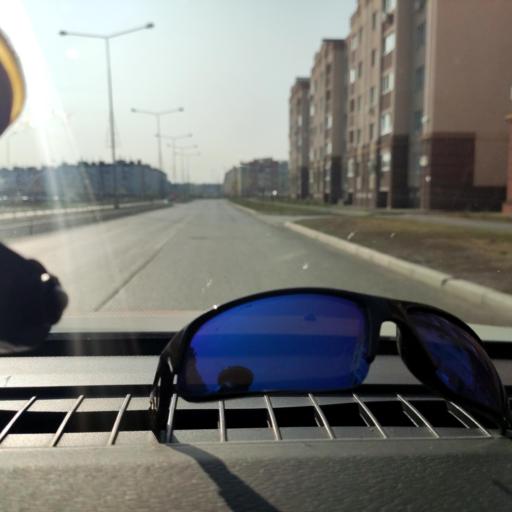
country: RU
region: Samara
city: Samara
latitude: 53.1166
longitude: 50.1560
